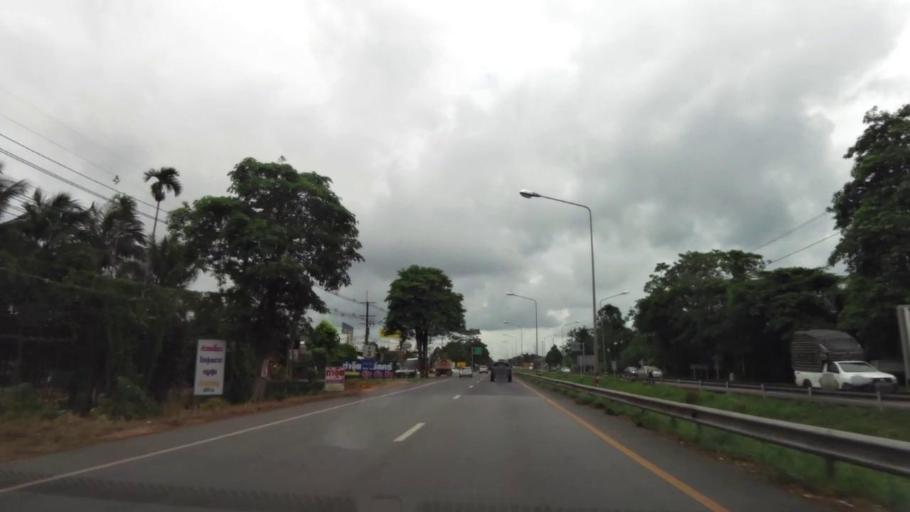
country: TH
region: Chanthaburi
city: Tha Mai
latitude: 12.6537
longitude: 102.0115
